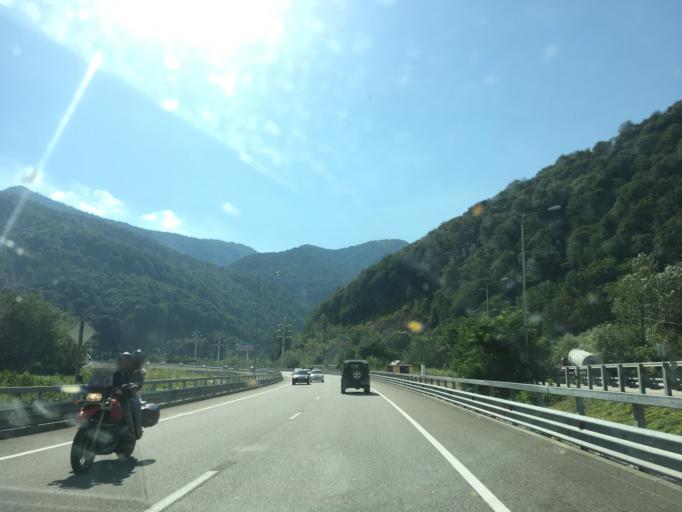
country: RU
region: Krasnodarskiy
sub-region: Sochi City
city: Krasnaya Polyana
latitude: 43.6161
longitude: 40.0588
